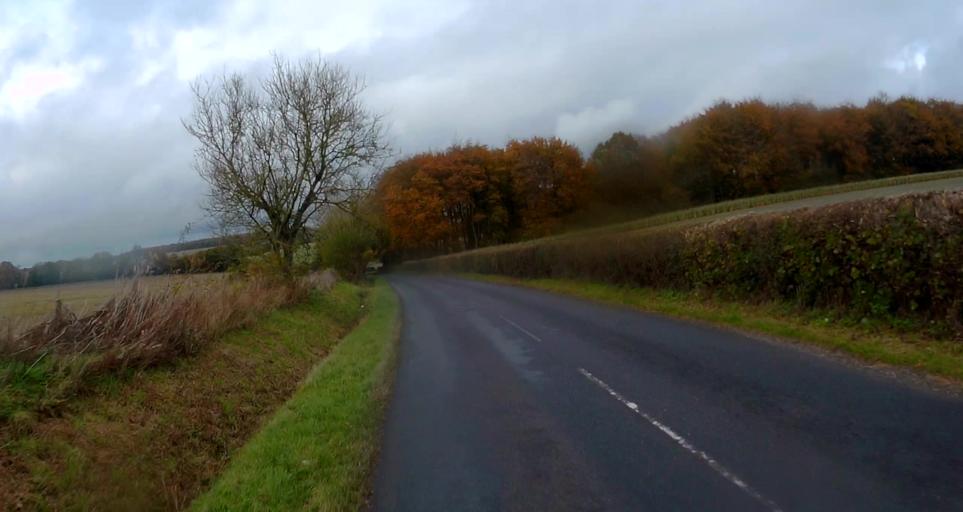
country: GB
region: England
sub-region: Hampshire
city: Four Marks
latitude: 51.1652
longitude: -1.0455
